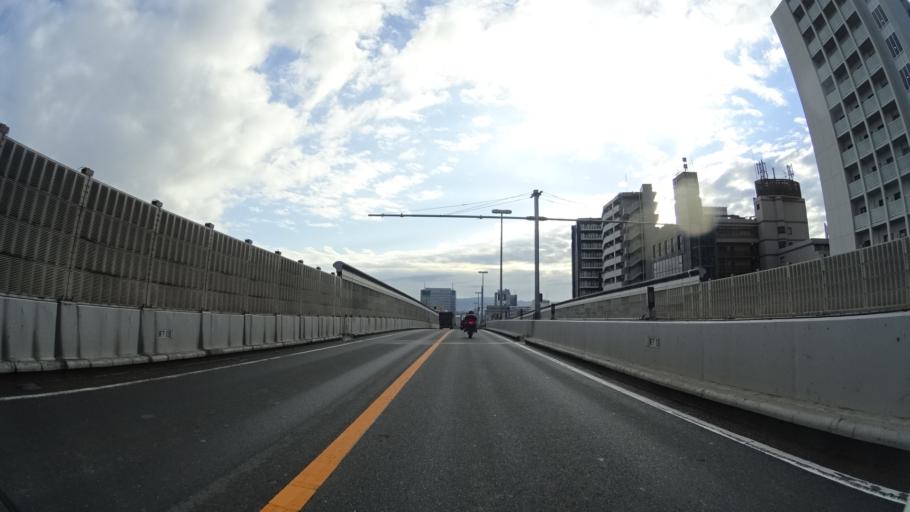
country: JP
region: Osaka
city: Osaka-shi
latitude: 34.6815
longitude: 135.5277
